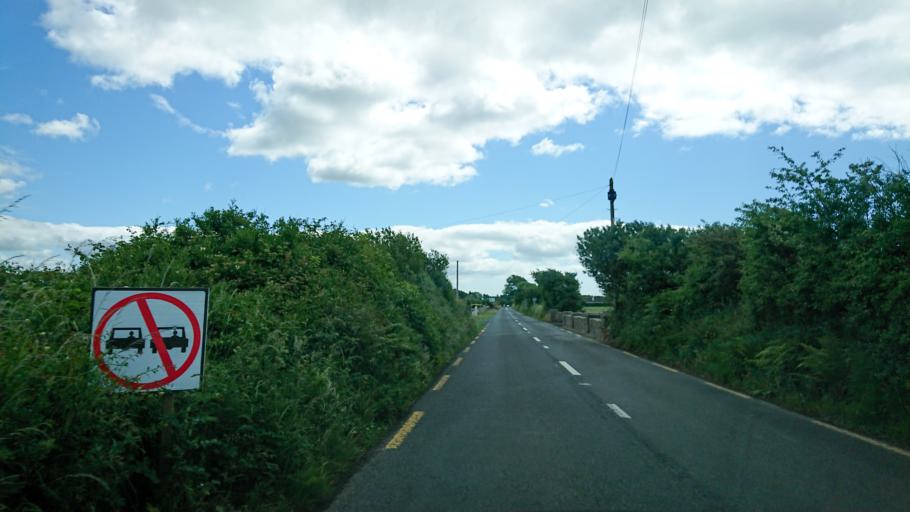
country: IE
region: Munster
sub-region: Waterford
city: Tra Mhor
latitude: 52.1796
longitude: -7.1658
